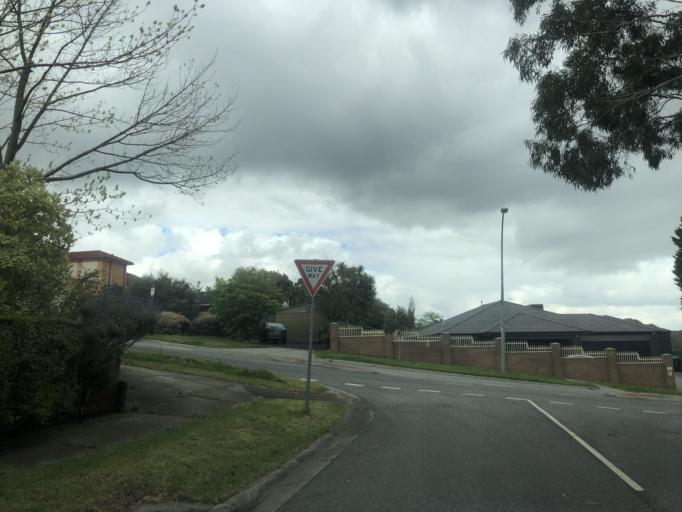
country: AU
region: Victoria
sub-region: Casey
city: Endeavour Hills
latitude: -37.9803
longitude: 145.2482
